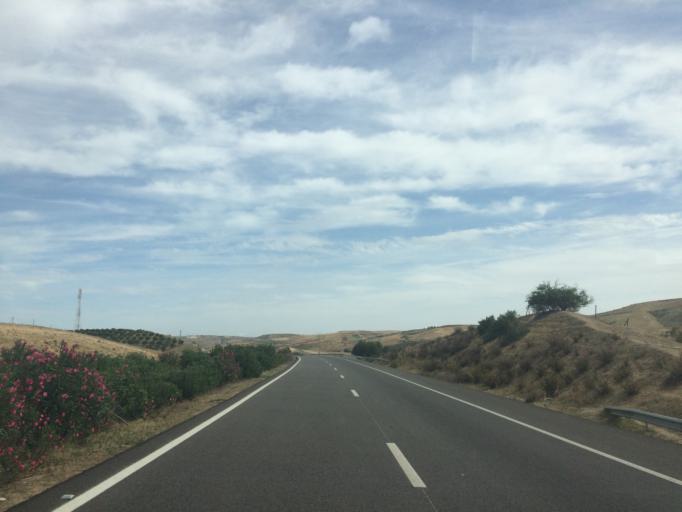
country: MA
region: Rabat-Sale-Zemmour-Zaer
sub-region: Khemisset
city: Khemisset
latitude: 33.8449
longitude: -5.8141
